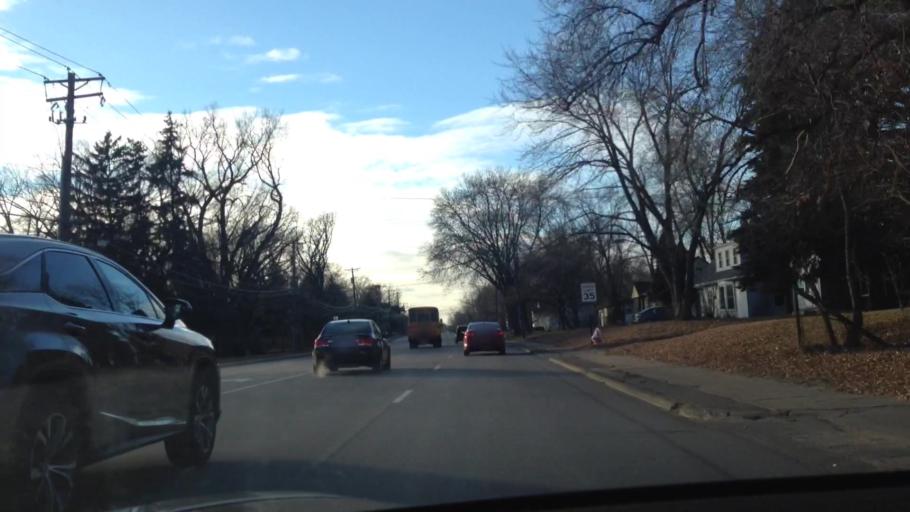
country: US
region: Minnesota
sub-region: Hennepin County
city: Crystal
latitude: 45.0328
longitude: -93.3609
